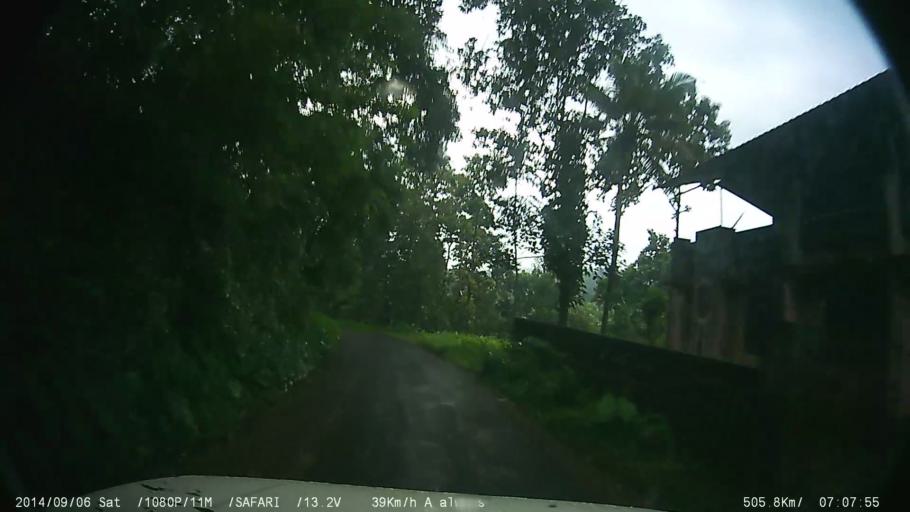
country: IN
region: Kerala
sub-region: Ernakulam
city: Piravam
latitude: 9.7948
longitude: 76.5404
